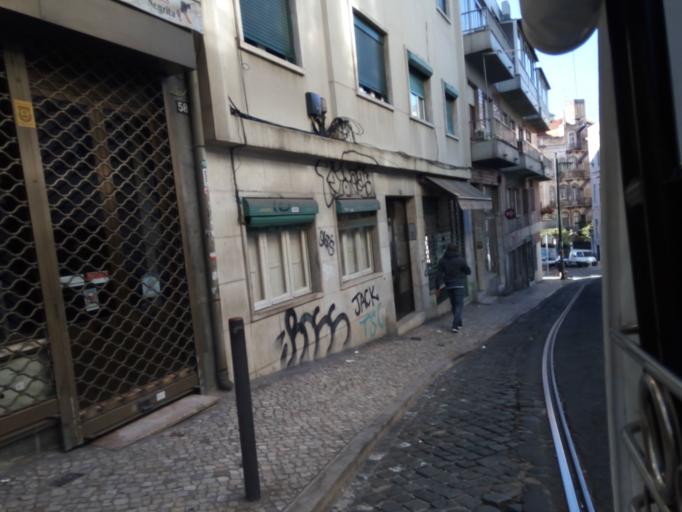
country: PT
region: Lisbon
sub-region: Lisbon
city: Lisbon
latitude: 38.7231
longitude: -9.1321
